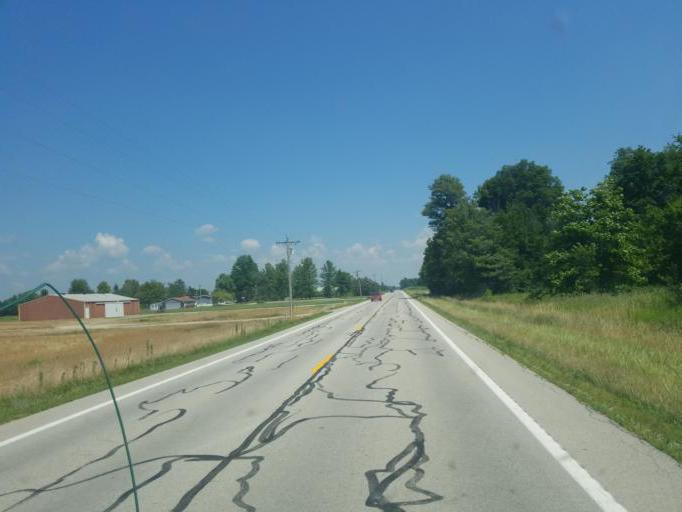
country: US
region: Ohio
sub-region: Shelby County
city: Jackson Center
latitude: 40.3959
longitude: -84.0732
